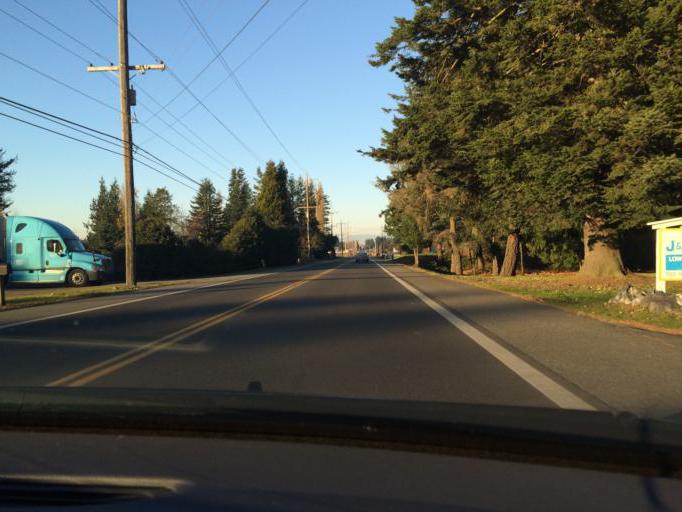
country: US
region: Washington
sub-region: Whatcom County
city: Lynden
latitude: 48.8959
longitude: -122.4424
